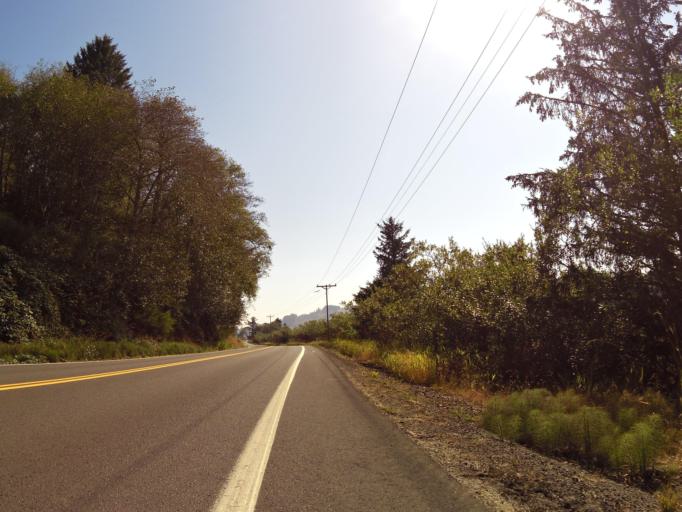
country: US
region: Oregon
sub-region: Tillamook County
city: Pacific City
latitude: 45.1850
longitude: -123.9461
